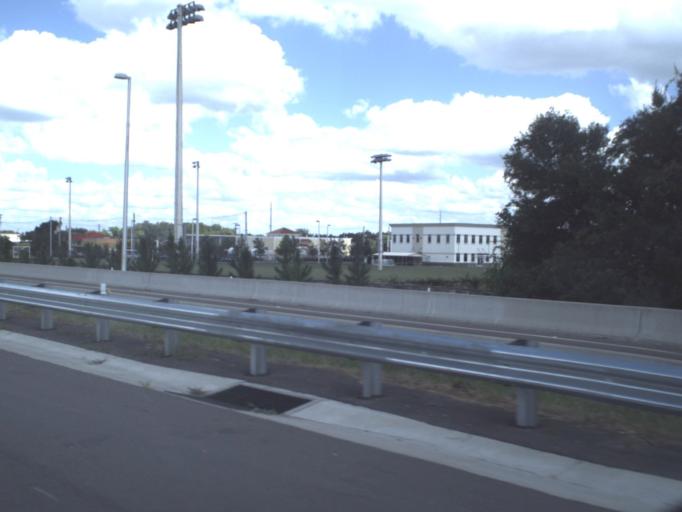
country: US
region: Florida
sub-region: Hillsborough County
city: Town 'n' Country
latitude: 28.0226
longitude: -82.5442
